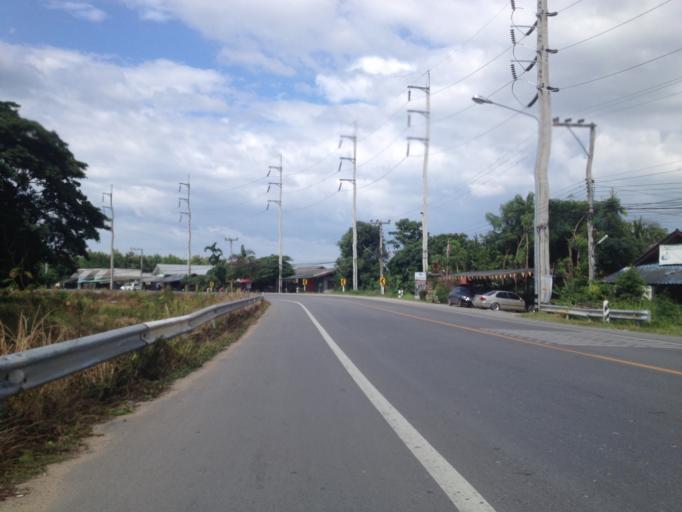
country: TH
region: Chiang Mai
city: Hang Dong
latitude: 18.6815
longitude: 98.8978
